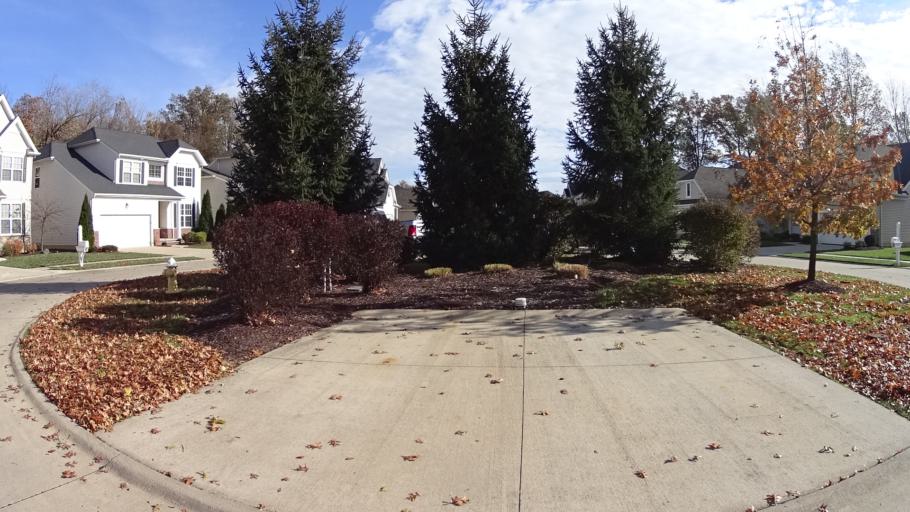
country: US
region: Ohio
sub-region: Lorain County
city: Avon Lake
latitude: 41.4941
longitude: -82.0427
